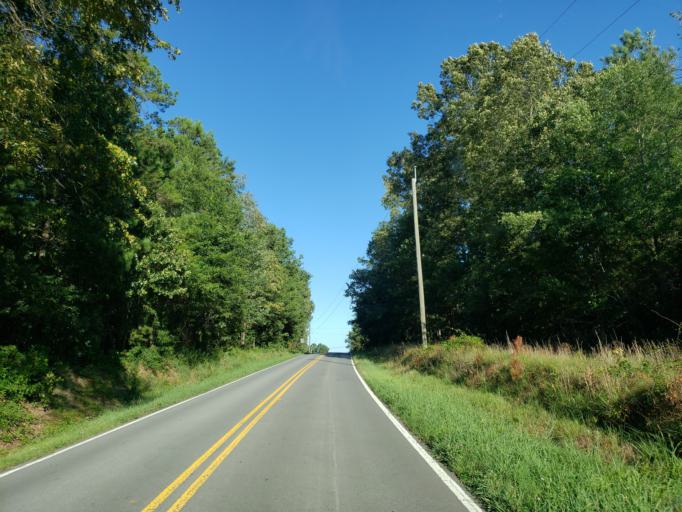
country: US
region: Georgia
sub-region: Polk County
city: Aragon
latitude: 34.1017
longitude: -85.0081
